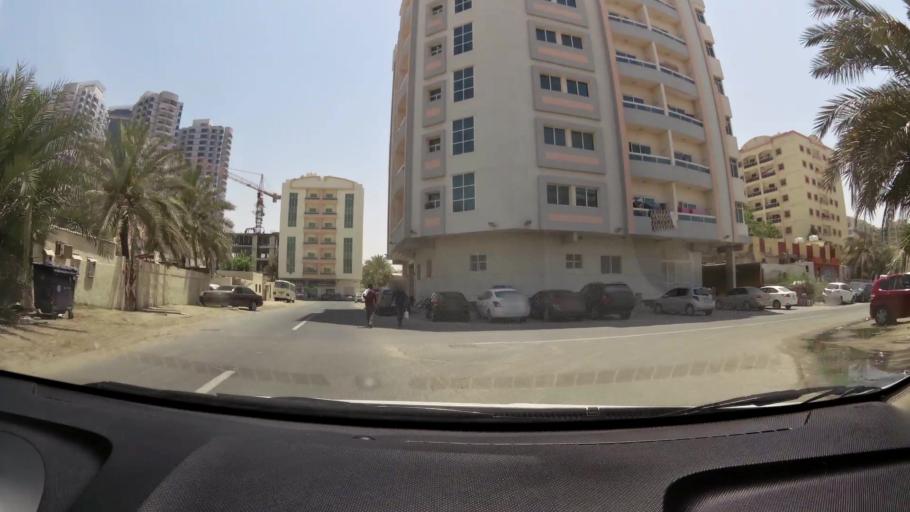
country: AE
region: Ajman
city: Ajman
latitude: 25.3963
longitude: 55.4471
